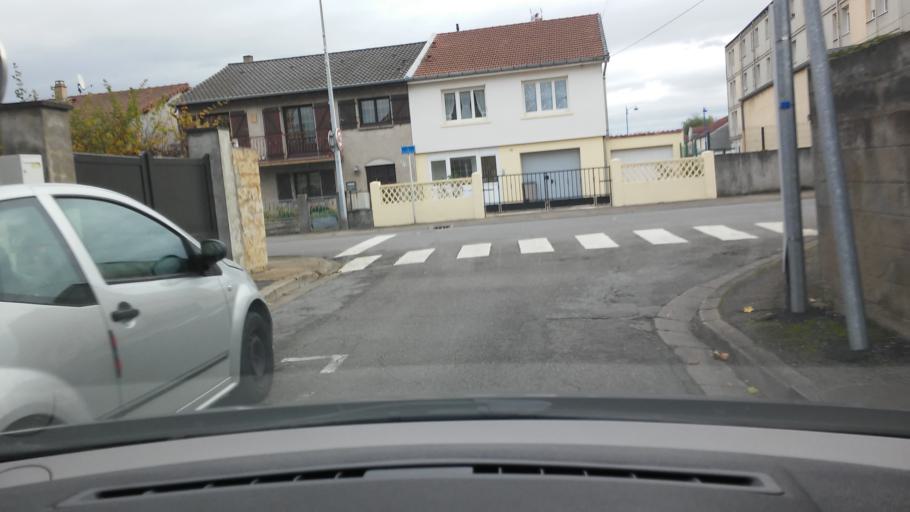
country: FR
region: Lorraine
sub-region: Departement de la Moselle
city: Talange
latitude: 49.2356
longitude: 6.1698
